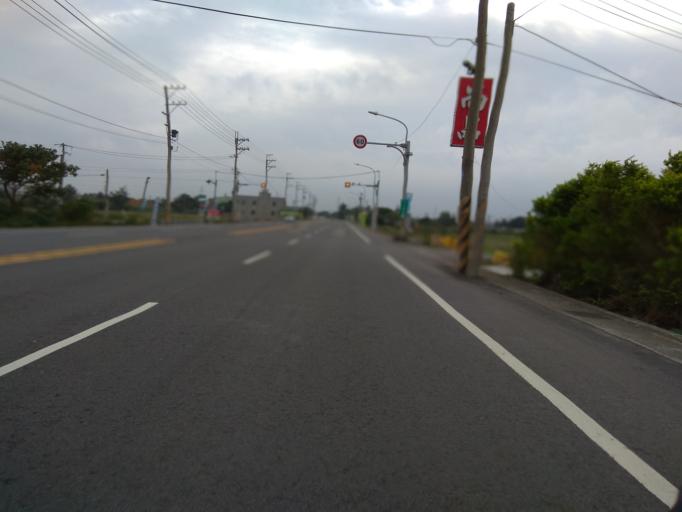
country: TW
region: Taiwan
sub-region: Hsinchu
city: Zhubei
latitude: 24.9839
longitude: 121.0562
